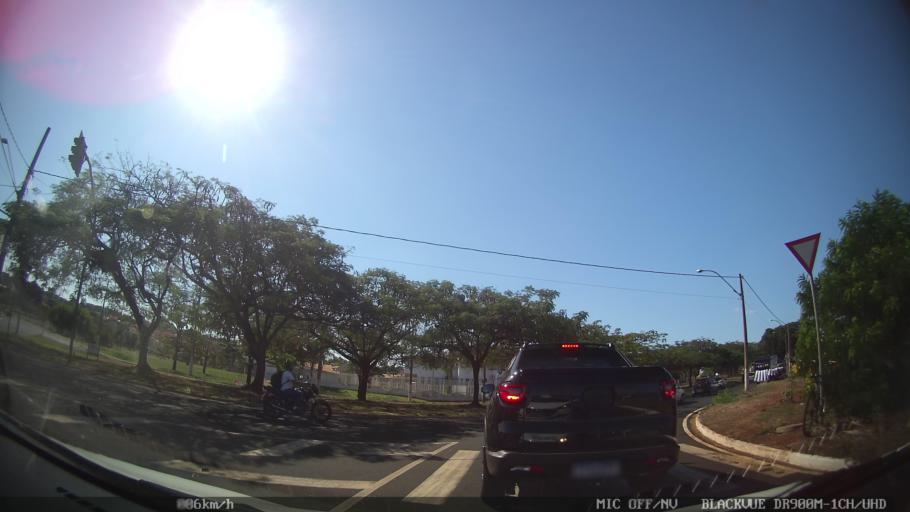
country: BR
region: Sao Paulo
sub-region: Ribeirao Preto
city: Ribeirao Preto
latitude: -21.2122
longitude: -47.7743
